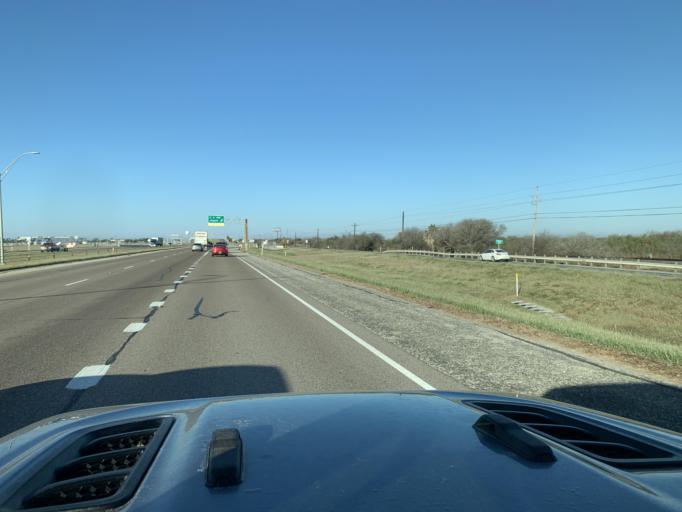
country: US
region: Texas
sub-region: Nueces County
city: Corpus Christi
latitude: 27.7851
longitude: -97.4939
